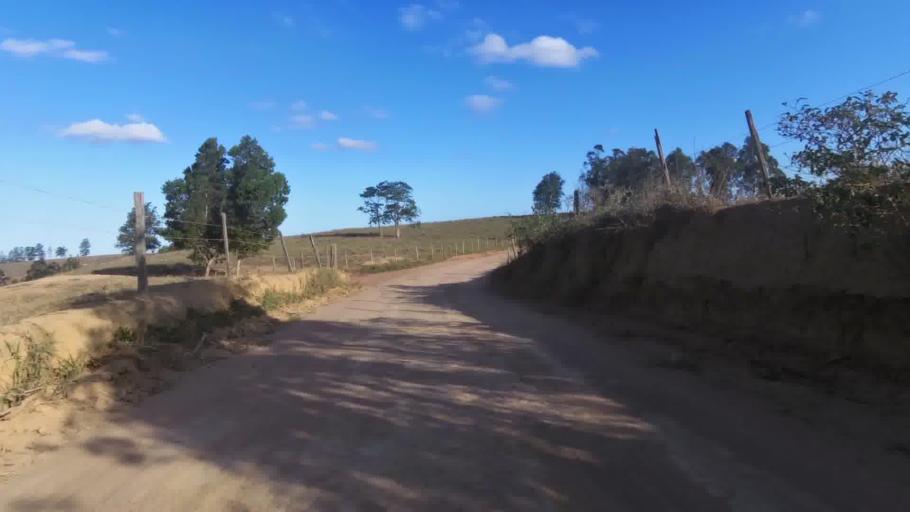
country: BR
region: Espirito Santo
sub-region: Marataizes
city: Marataizes
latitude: -21.1641
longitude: -41.0565
